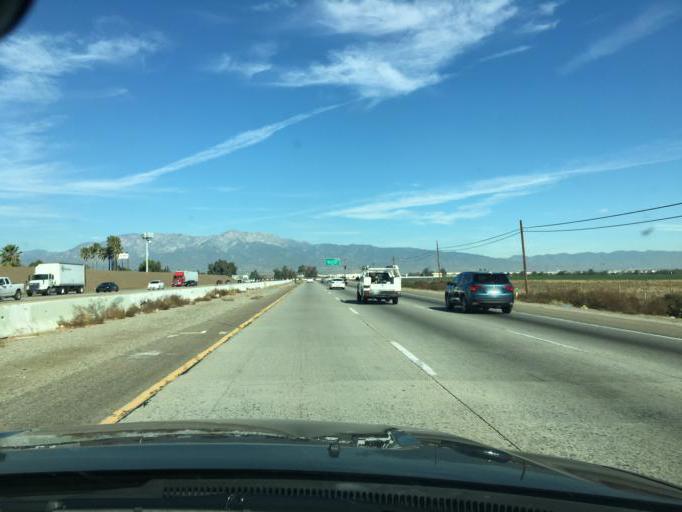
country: US
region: California
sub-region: Riverside County
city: Mira Loma
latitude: 33.9821
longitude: -117.5488
